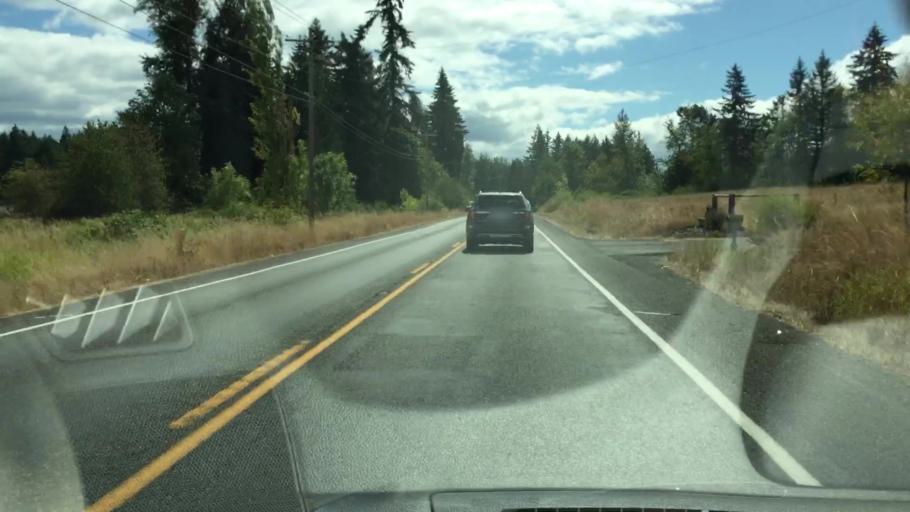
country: US
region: Washington
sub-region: Pierce County
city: Eatonville
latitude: 46.8830
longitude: -122.3009
